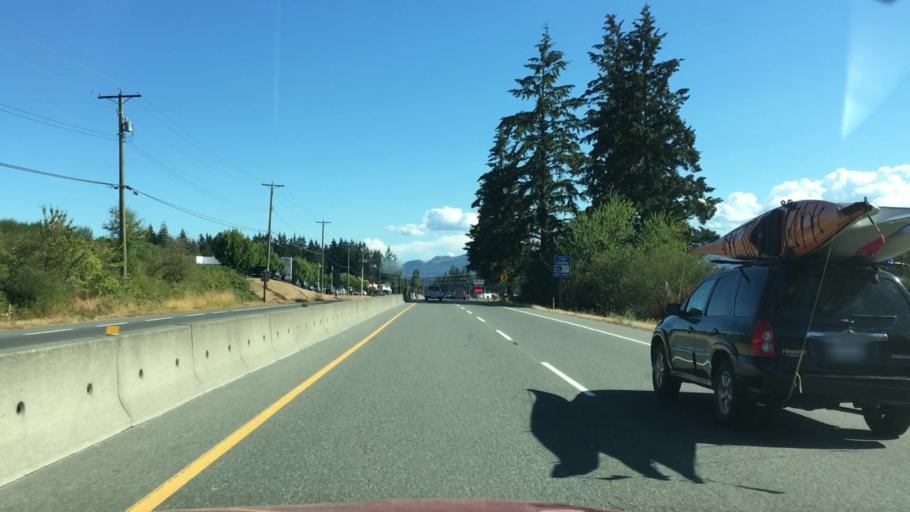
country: CA
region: British Columbia
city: Duncan
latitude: 48.8087
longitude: -123.7173
